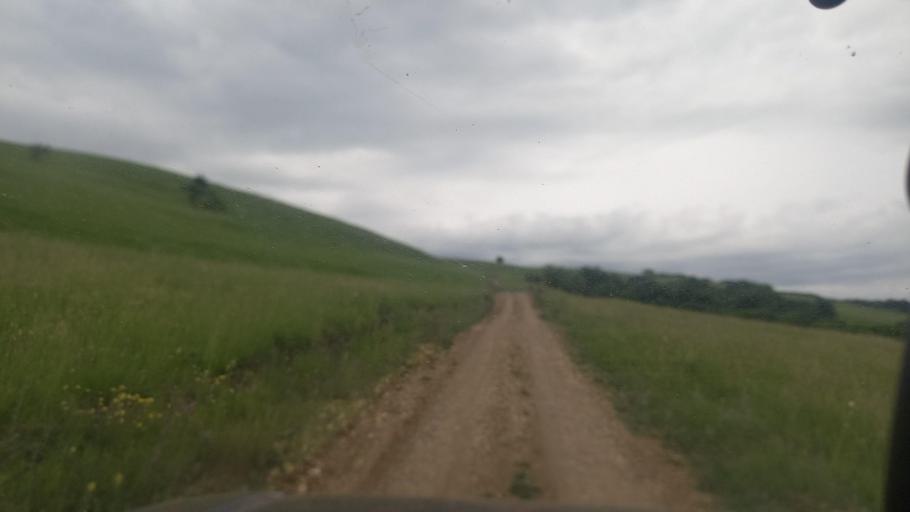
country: RU
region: Krasnodarskiy
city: Peredovaya
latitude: 44.0777
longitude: 41.3638
